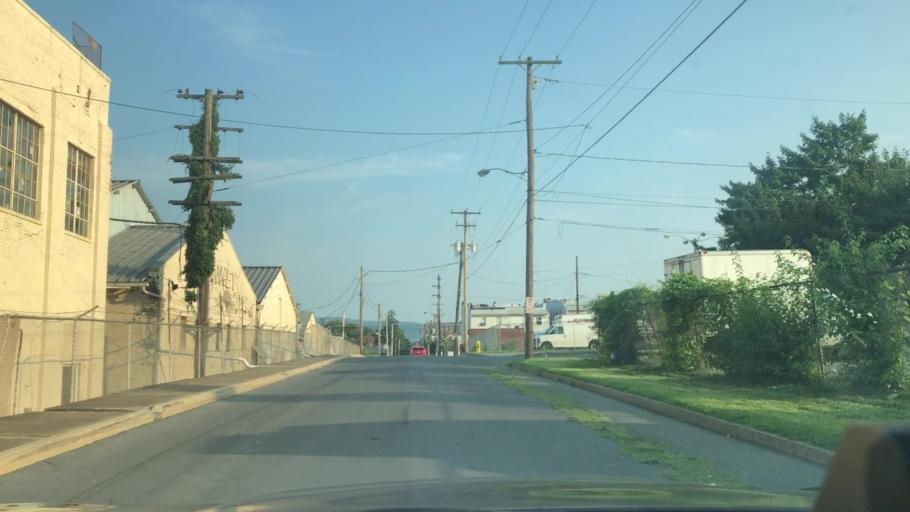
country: US
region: Pennsylvania
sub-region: Lehigh County
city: Fullerton
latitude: 40.6177
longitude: -75.4697
